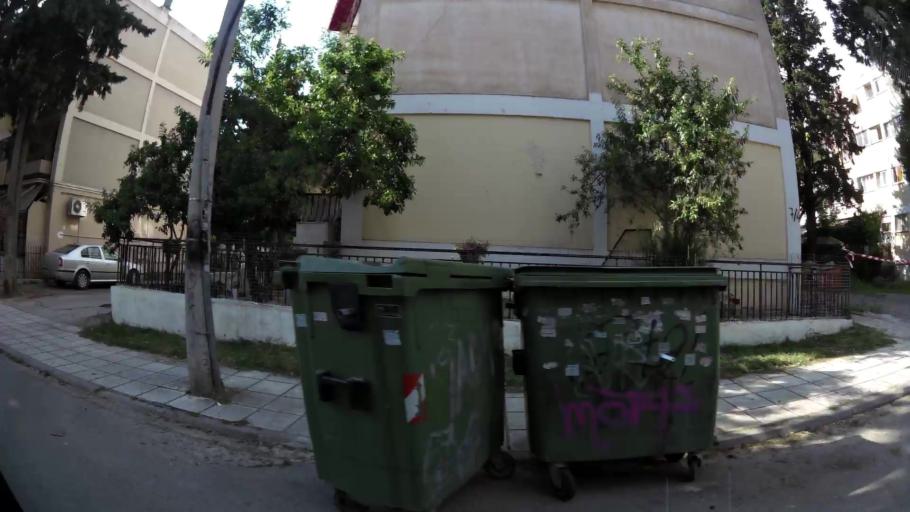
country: GR
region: Central Macedonia
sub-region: Nomos Thessalonikis
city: Kalamaria
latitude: 40.5699
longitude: 22.9741
